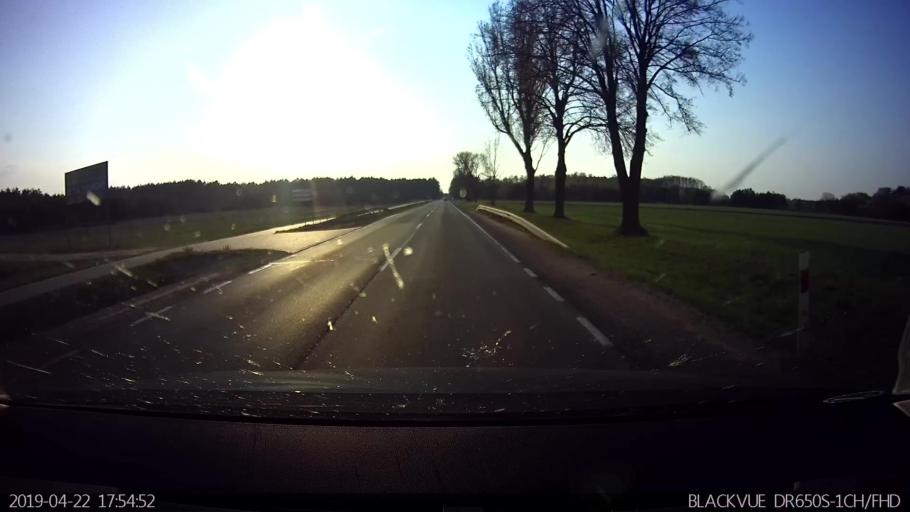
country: PL
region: Masovian Voivodeship
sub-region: Powiat wegrowski
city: Stoczek
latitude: 52.4595
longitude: 21.9299
